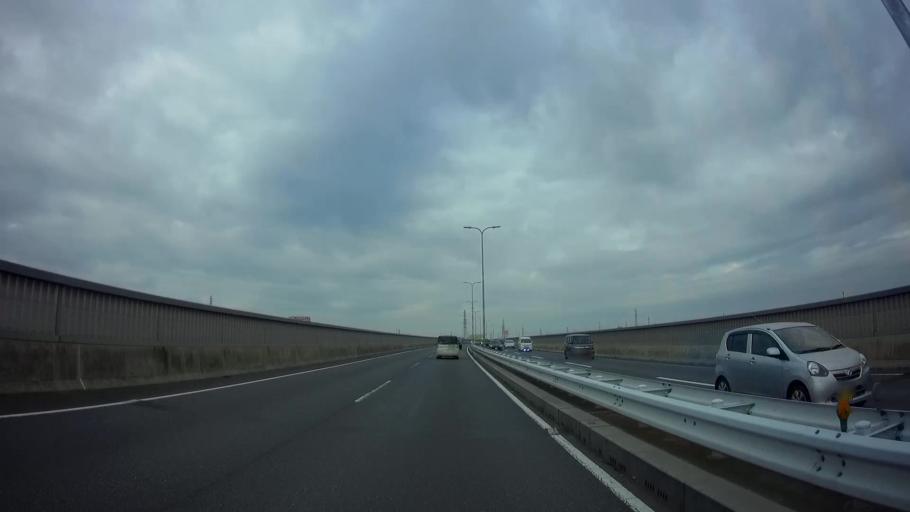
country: JP
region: Saitama
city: Kumagaya
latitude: 36.1657
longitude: 139.3866
